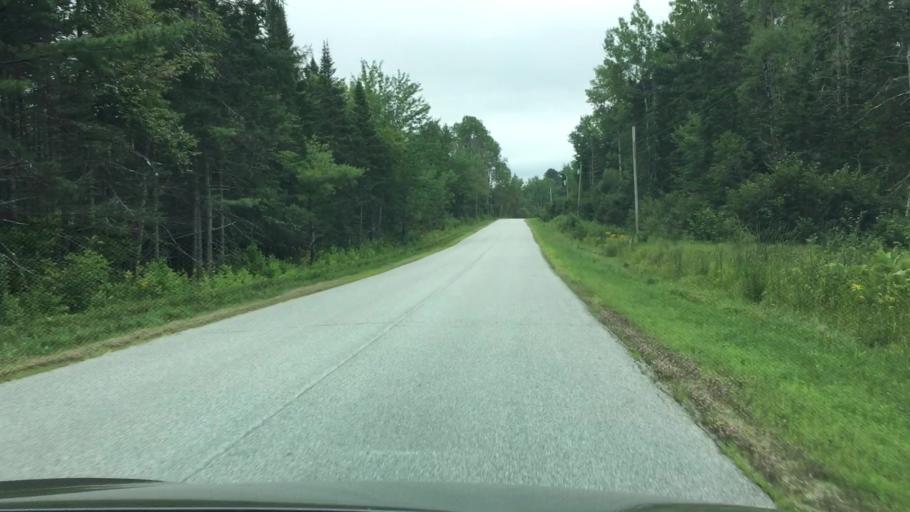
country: US
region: Maine
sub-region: Waldo County
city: Stockton Springs
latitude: 44.5288
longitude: -68.8306
